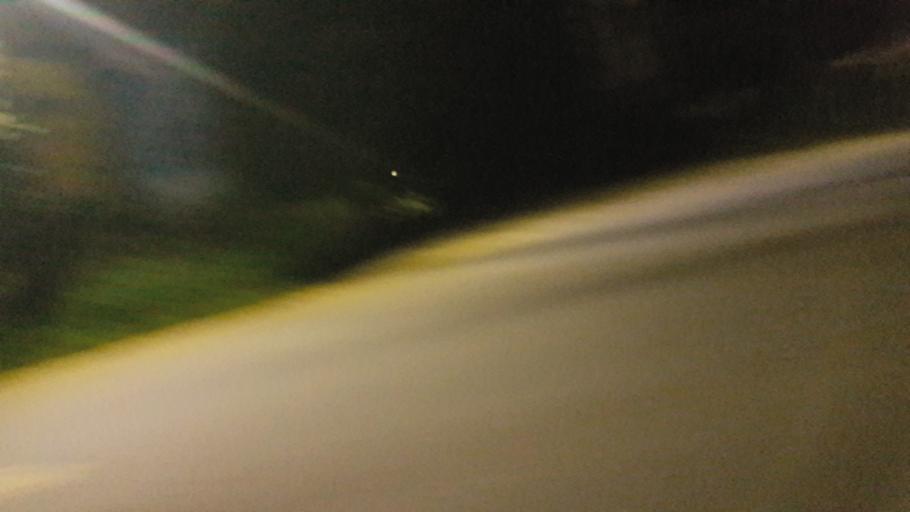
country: TW
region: Taiwan
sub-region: Hsinchu
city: Hsinchu
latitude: 24.7700
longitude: 120.9771
